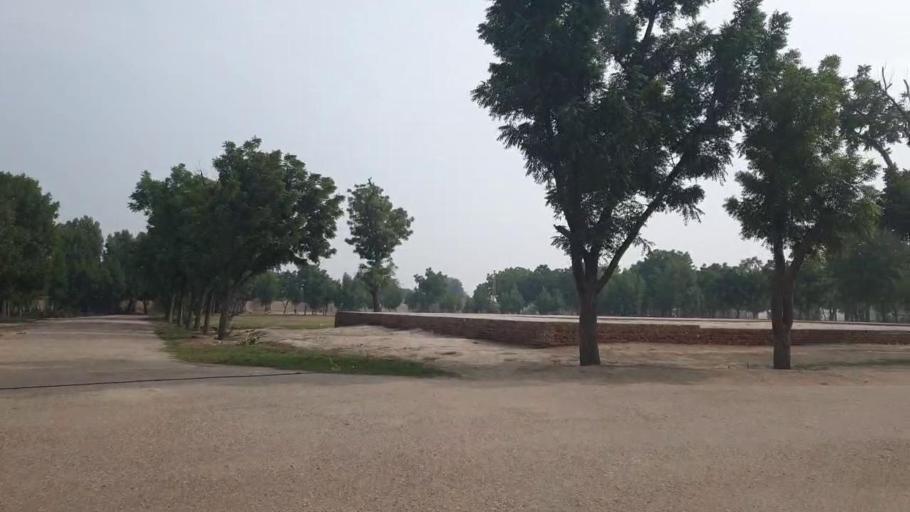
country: PK
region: Sindh
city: Sann
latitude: 26.0397
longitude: 68.1405
